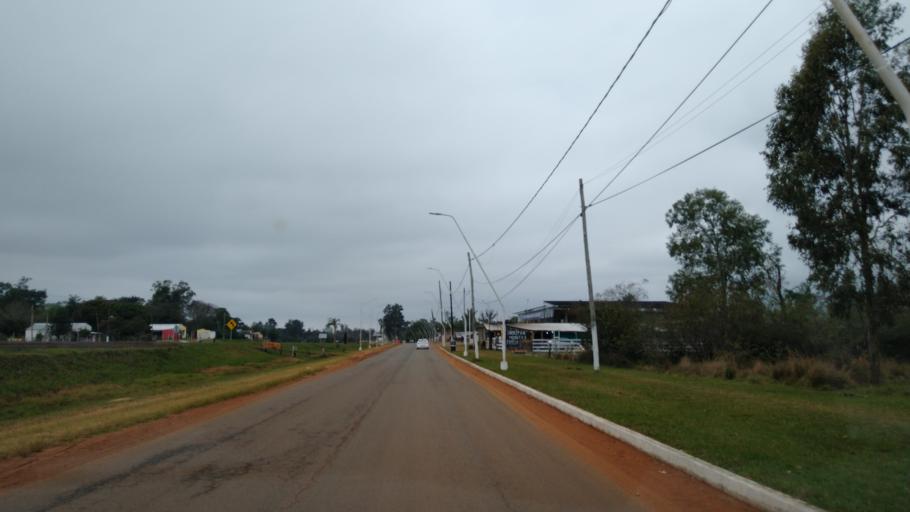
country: AR
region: Corrientes
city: Alvear
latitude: -29.0865
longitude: -56.5558
